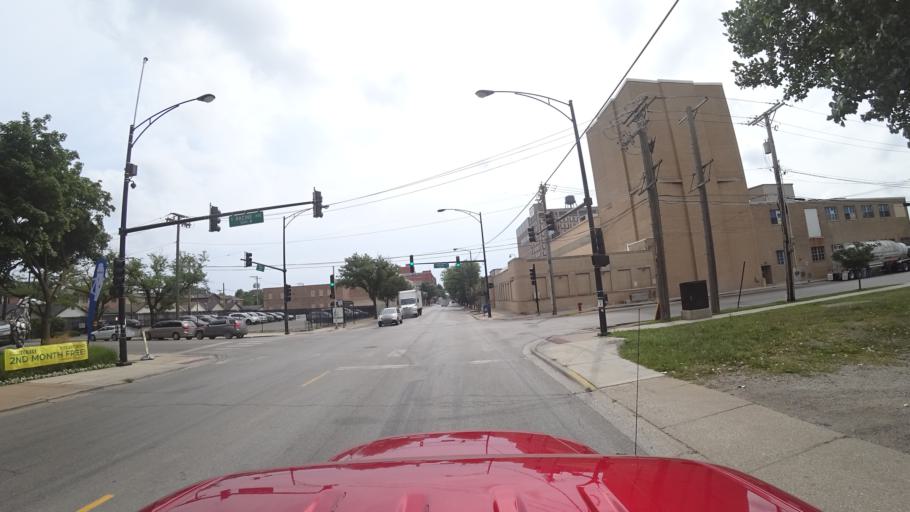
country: US
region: Illinois
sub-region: Cook County
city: Chicago
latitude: 41.8306
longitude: -87.6561
